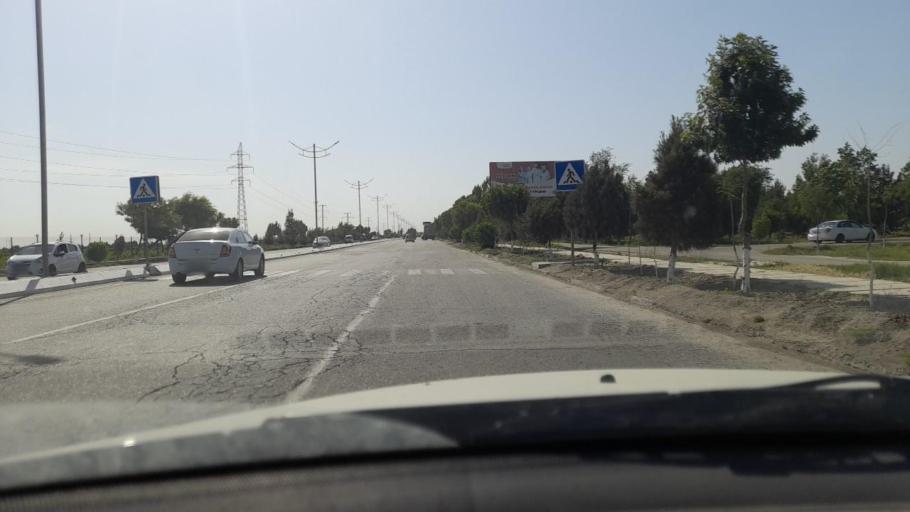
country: UZ
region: Bukhara
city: Bukhara
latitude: 39.8011
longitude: 64.4312
